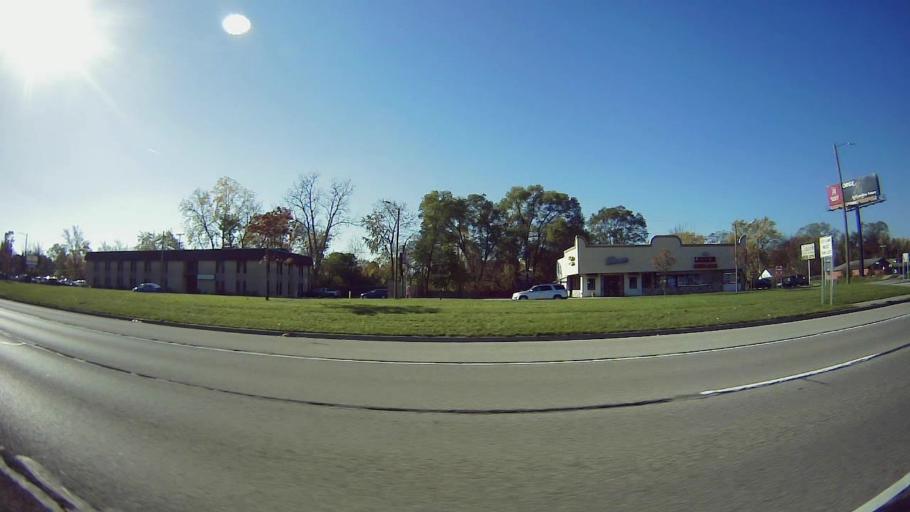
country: US
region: Michigan
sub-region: Wayne County
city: Redford
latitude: 42.4188
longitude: -83.2771
